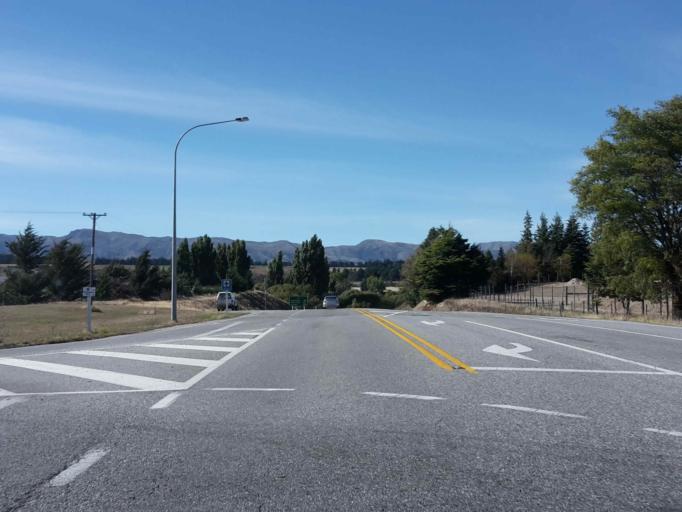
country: NZ
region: Otago
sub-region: Queenstown-Lakes District
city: Wanaka
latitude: -44.6967
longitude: 169.1712
